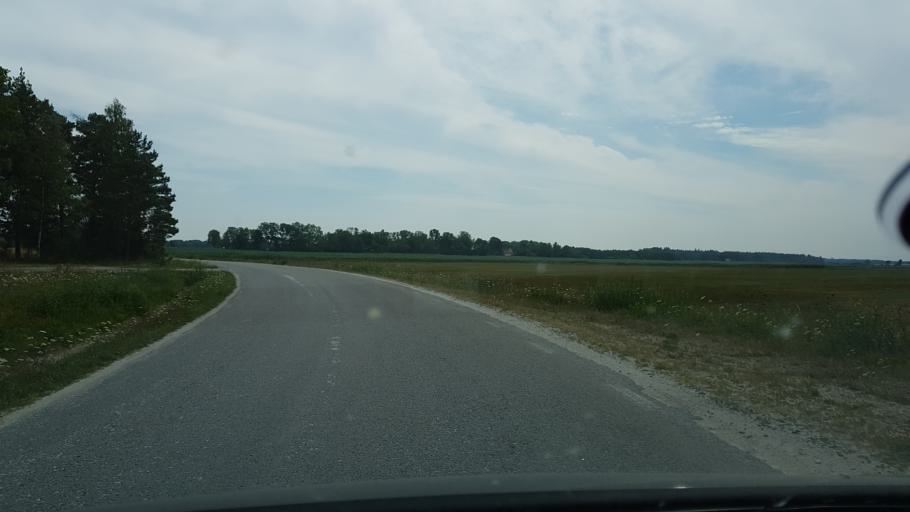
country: SE
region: Gotland
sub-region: Gotland
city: Visby
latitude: 57.7083
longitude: 18.5061
